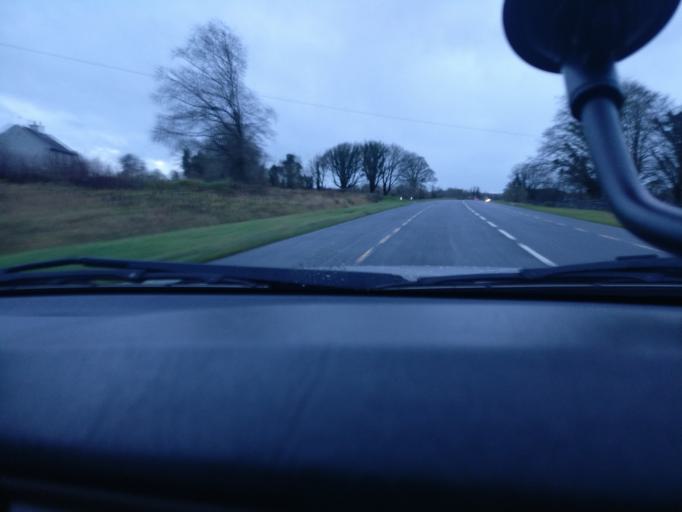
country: IE
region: Connaught
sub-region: County Galway
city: Ballinasloe
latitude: 53.2946
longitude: -8.3281
